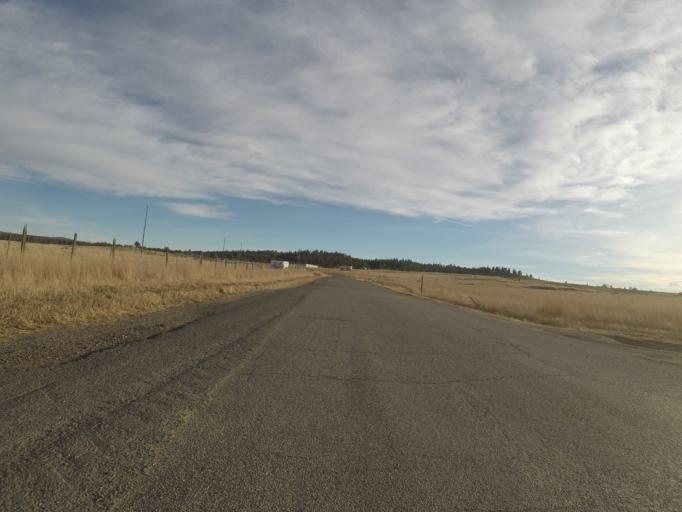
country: US
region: Montana
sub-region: Musselshell County
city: Roundup
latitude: 46.3068
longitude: -108.8130
